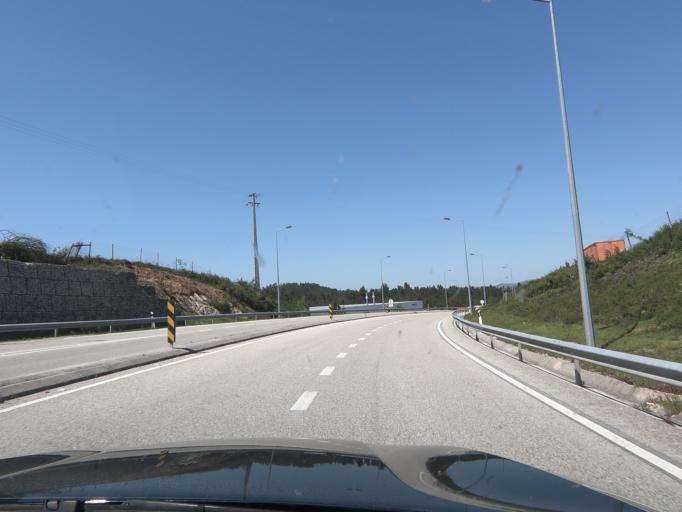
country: PT
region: Coimbra
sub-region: Lousa
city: Lousa
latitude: 40.1131
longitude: -8.2918
